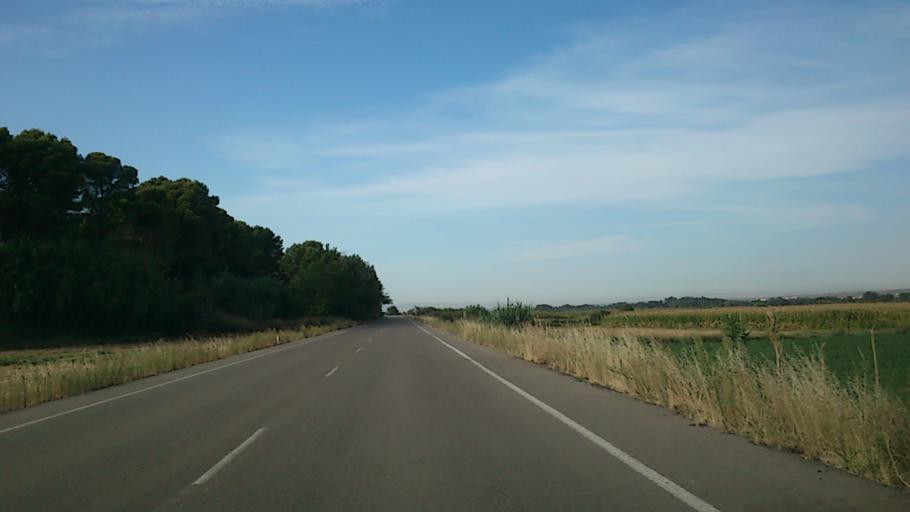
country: ES
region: Aragon
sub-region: Provincia de Zaragoza
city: Villanueva de Gallego
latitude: 41.7887
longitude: -0.7846
